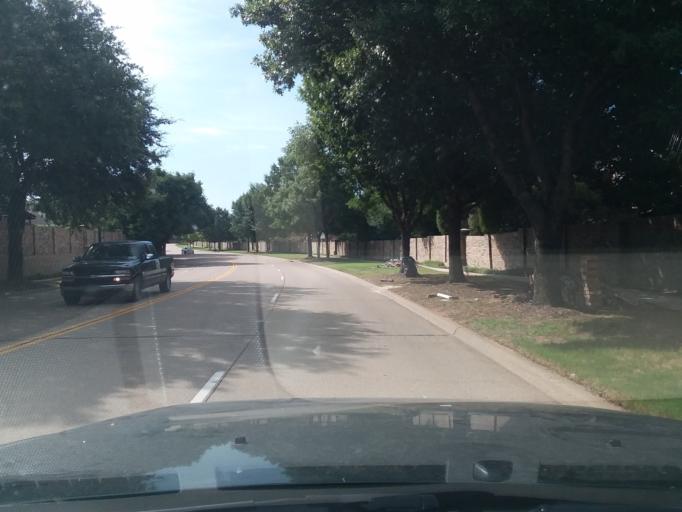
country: US
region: Texas
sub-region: Denton County
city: Flower Mound
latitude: 33.0251
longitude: -97.0907
